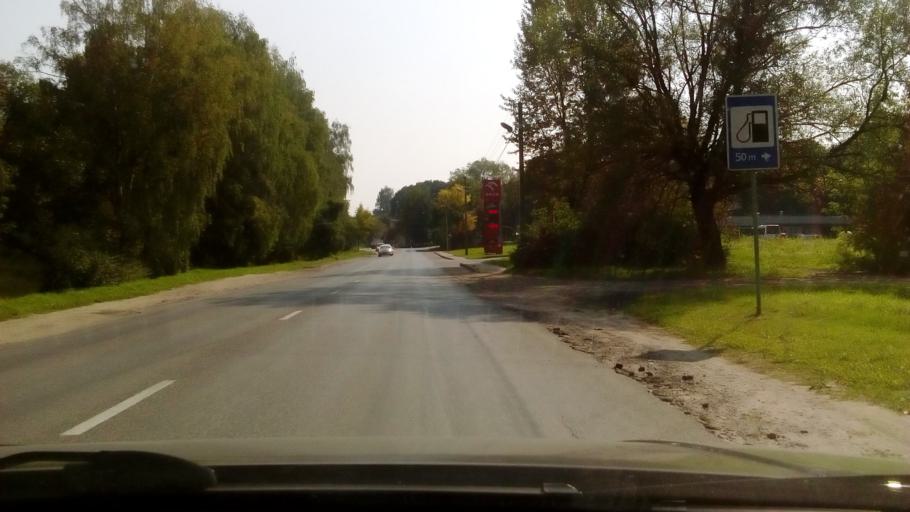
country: LT
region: Alytaus apskritis
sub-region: Alytus
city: Alytus
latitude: 54.4042
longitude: 24.0364
